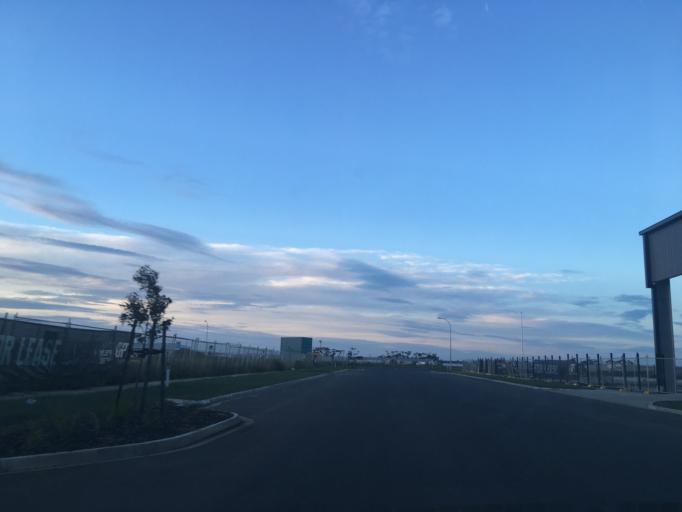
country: AU
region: Victoria
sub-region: Wyndham
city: Truganina
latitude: -37.8327
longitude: 144.7403
